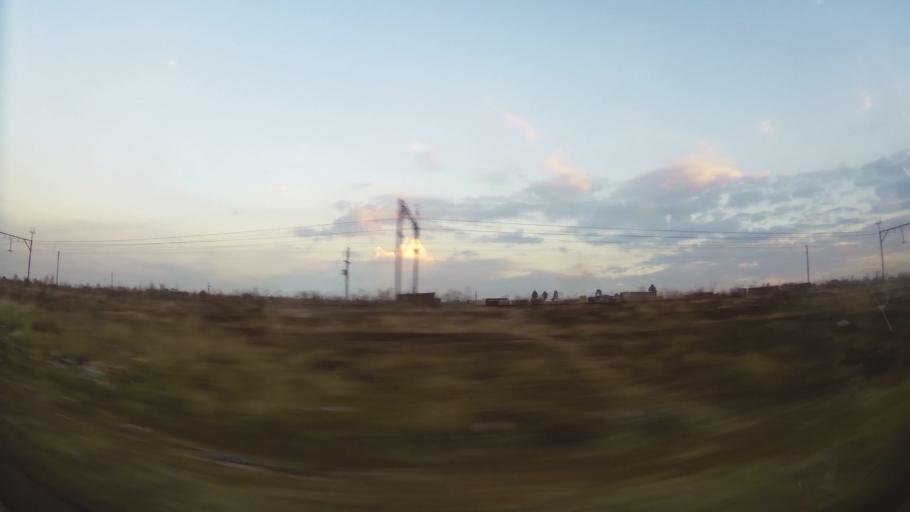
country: ZA
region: Gauteng
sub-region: City of Johannesburg Metropolitan Municipality
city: Orange Farm
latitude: -26.5627
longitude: 27.8702
